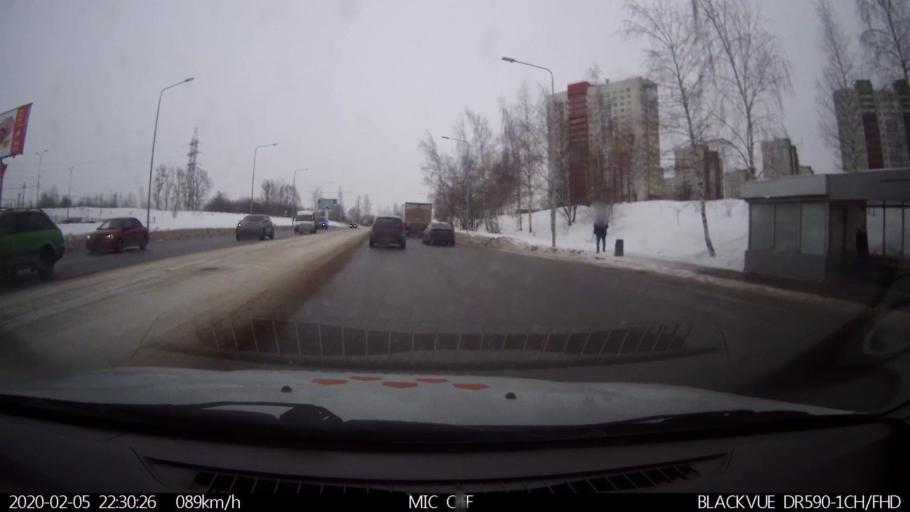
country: RU
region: Nizjnij Novgorod
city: Imeni Stepana Razina
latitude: 54.7430
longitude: 44.1611
